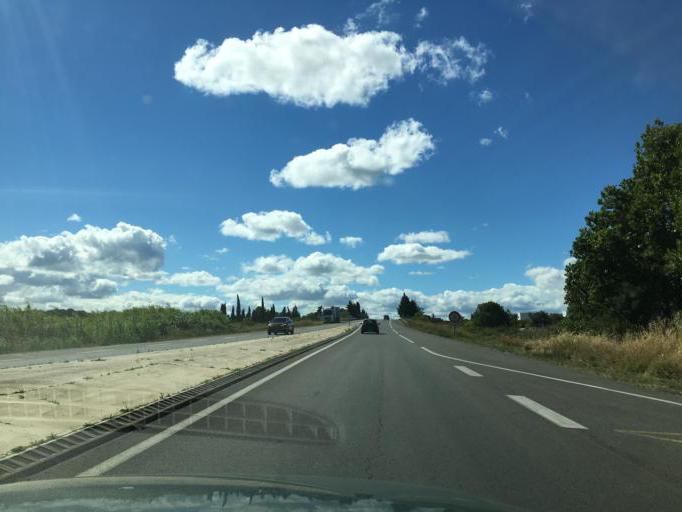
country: FR
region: Languedoc-Roussillon
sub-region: Departement de l'Herault
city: Meze
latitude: 43.4403
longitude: 3.5765
